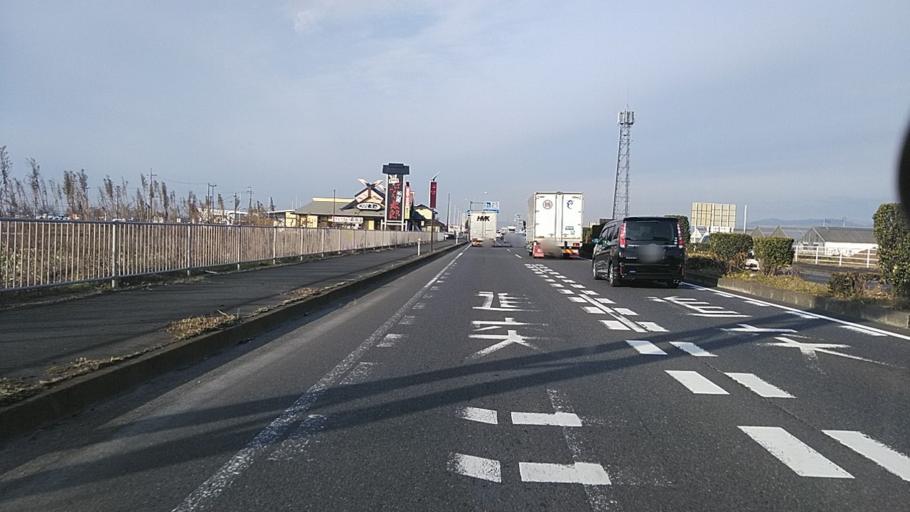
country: JP
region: Tochigi
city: Oyama
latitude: 36.3087
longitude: 139.7642
